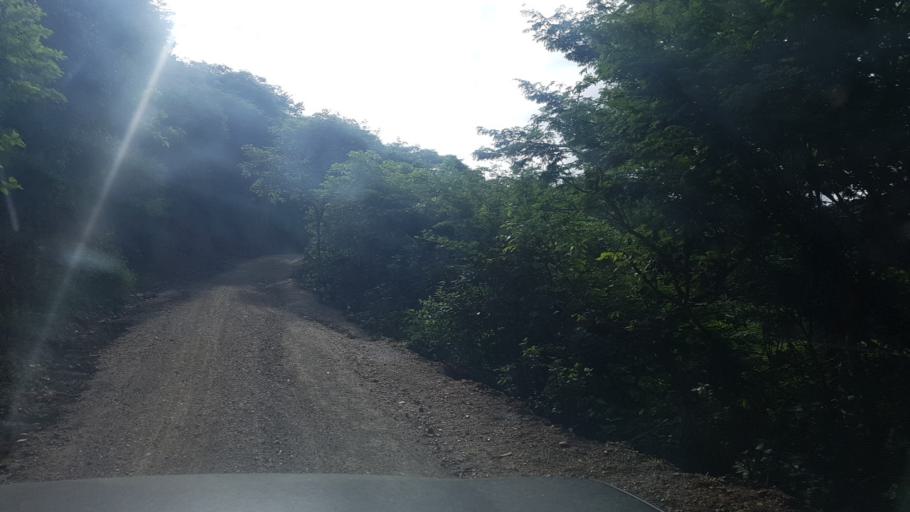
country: NI
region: Nueva Segovia
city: Ocotal
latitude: 13.6025
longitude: -86.4425
